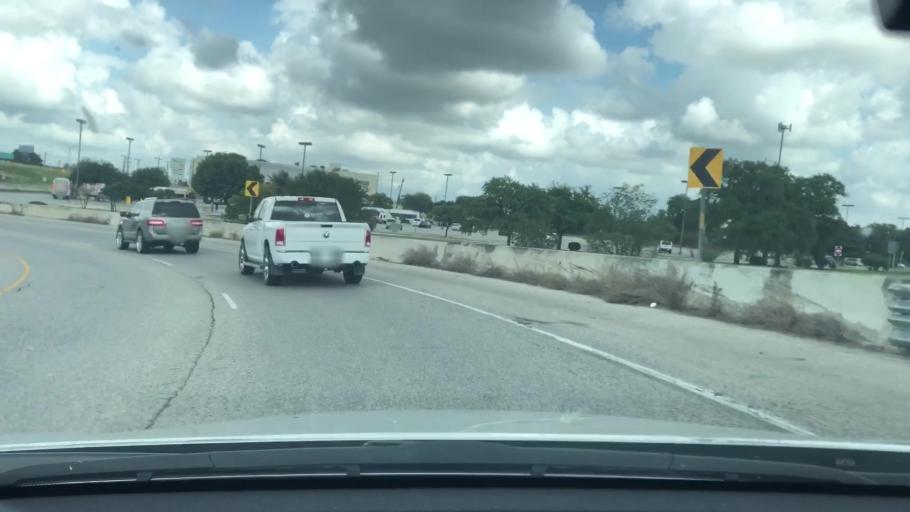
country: US
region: Texas
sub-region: Bexar County
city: Windcrest
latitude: 29.5227
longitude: -98.3923
